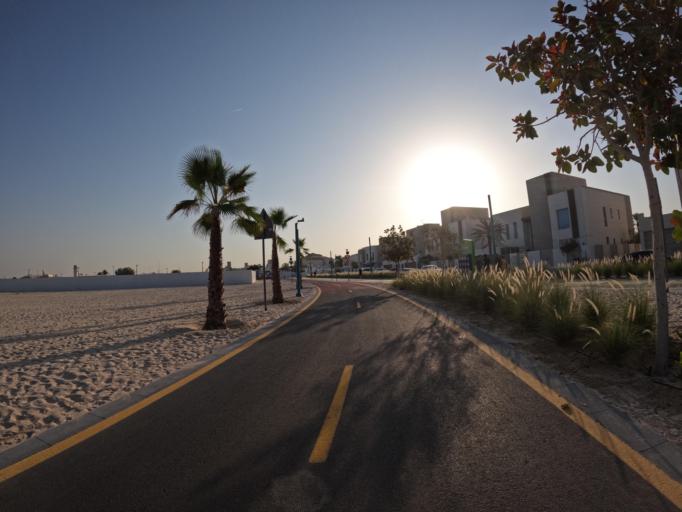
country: AE
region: Dubai
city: Dubai
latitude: 25.1703
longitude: 55.2120
